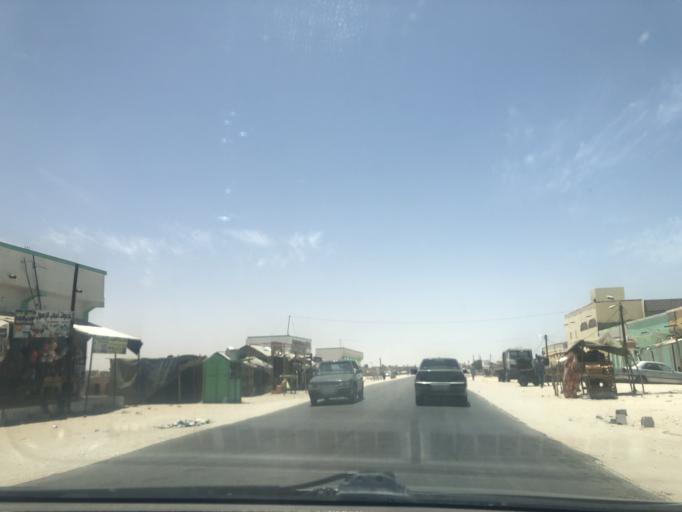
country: MR
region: Nouakchott
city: Nouakchott
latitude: 18.0142
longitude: -15.9591
